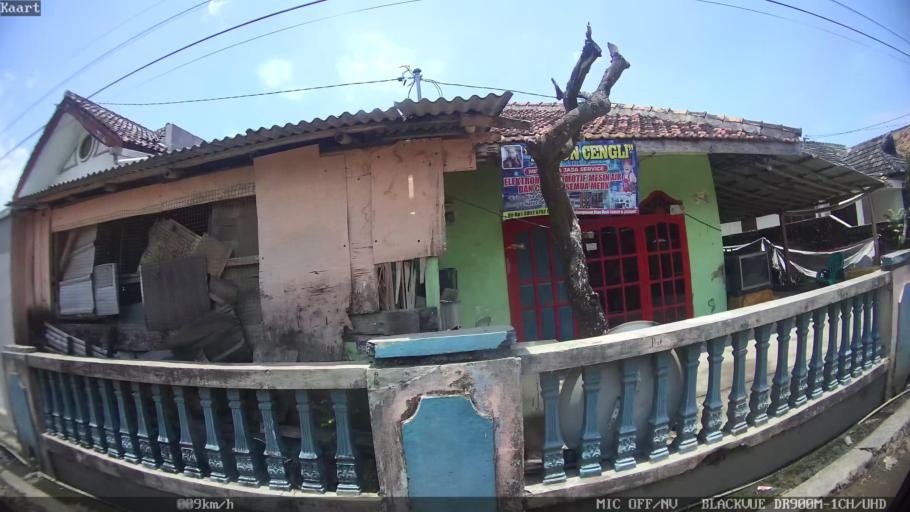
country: ID
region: Lampung
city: Kedaton
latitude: -5.3807
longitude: 105.2946
